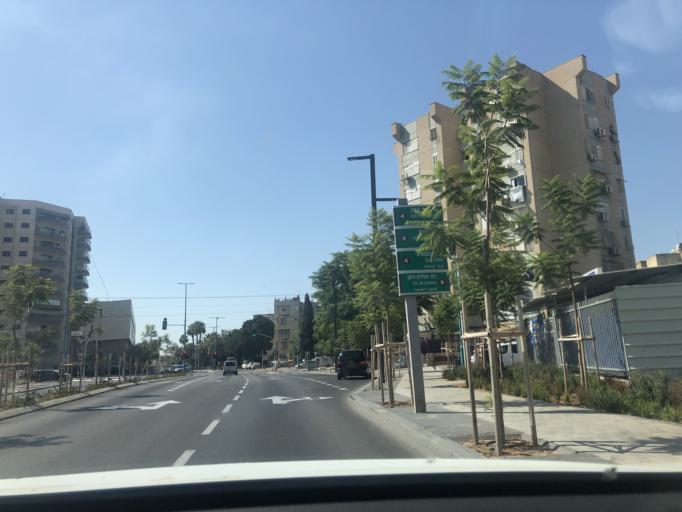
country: IL
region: Central District
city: Lod
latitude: 31.9444
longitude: 34.8949
